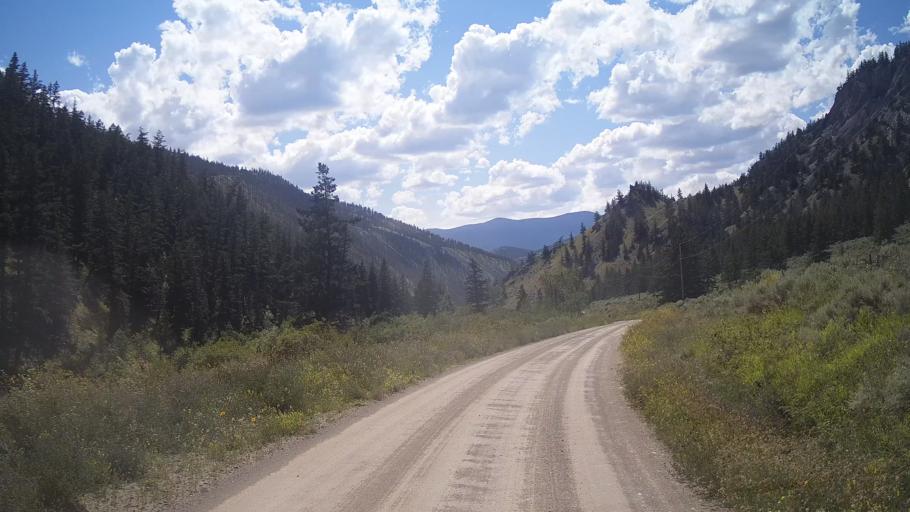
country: CA
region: British Columbia
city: Lillooet
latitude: 51.2325
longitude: -122.0534
